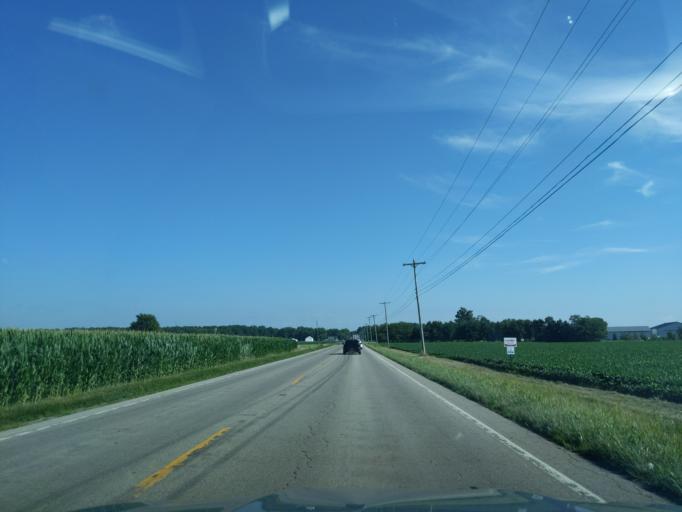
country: US
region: Indiana
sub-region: Ripley County
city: Osgood
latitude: 39.1604
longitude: -85.3068
